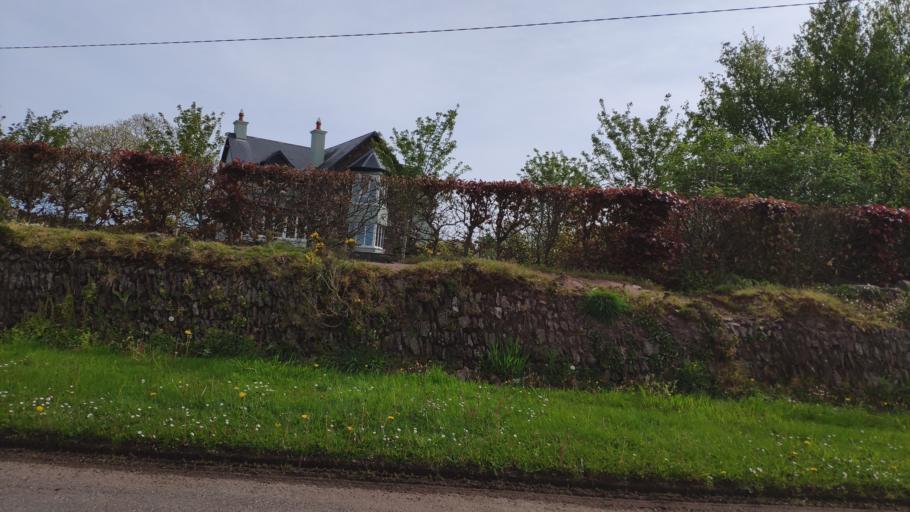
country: IE
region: Munster
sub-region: County Cork
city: Blarney
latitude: 51.9601
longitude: -8.5125
